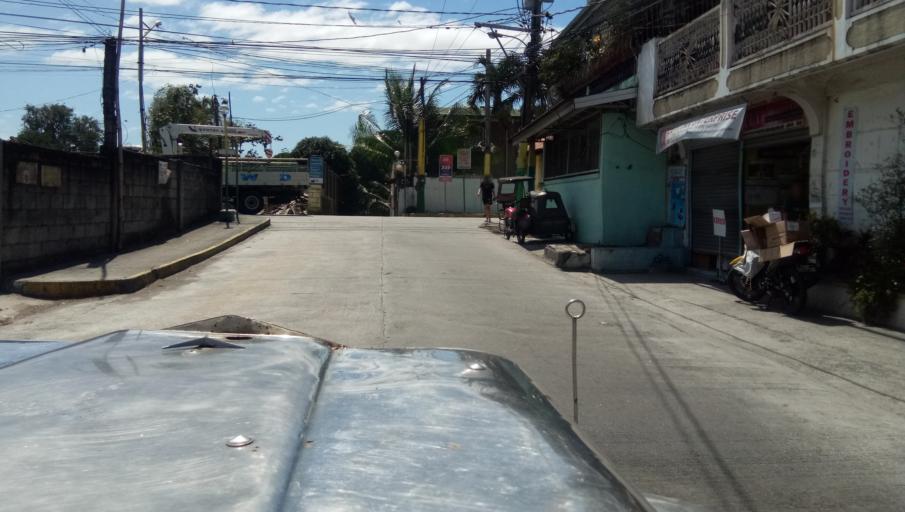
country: PH
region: Calabarzon
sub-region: Province of Cavite
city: Dasmarinas
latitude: 14.3288
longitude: 120.9334
